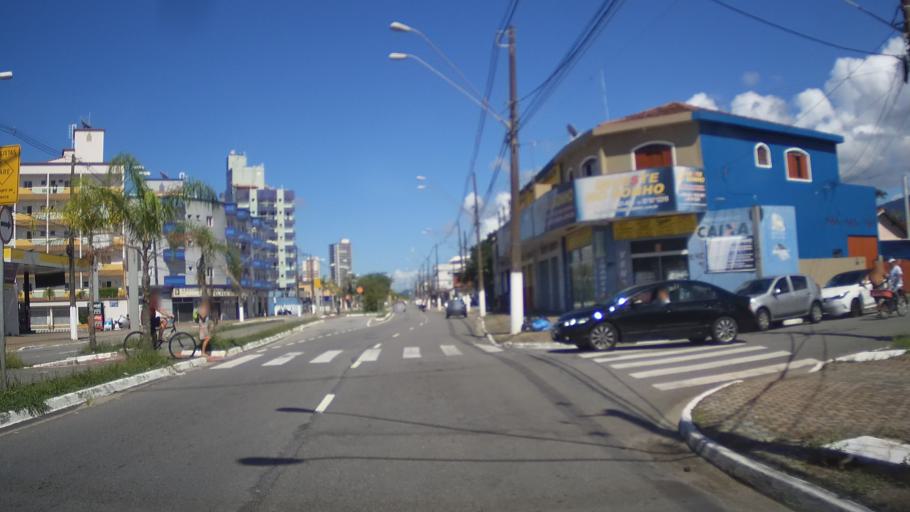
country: BR
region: Sao Paulo
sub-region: Mongagua
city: Mongagua
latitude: -24.0428
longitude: -46.5208
